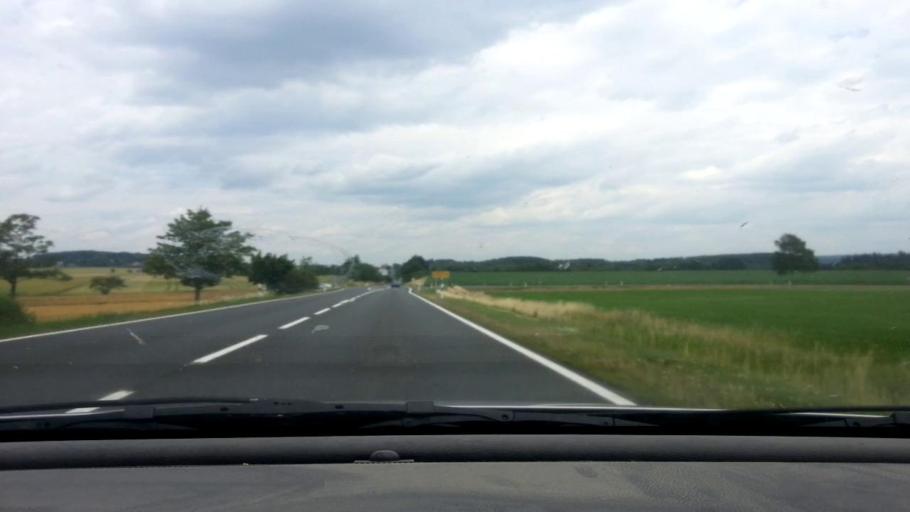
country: DE
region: Bavaria
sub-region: Upper Palatinate
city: Mitterteich
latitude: 49.9670
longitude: 12.2597
